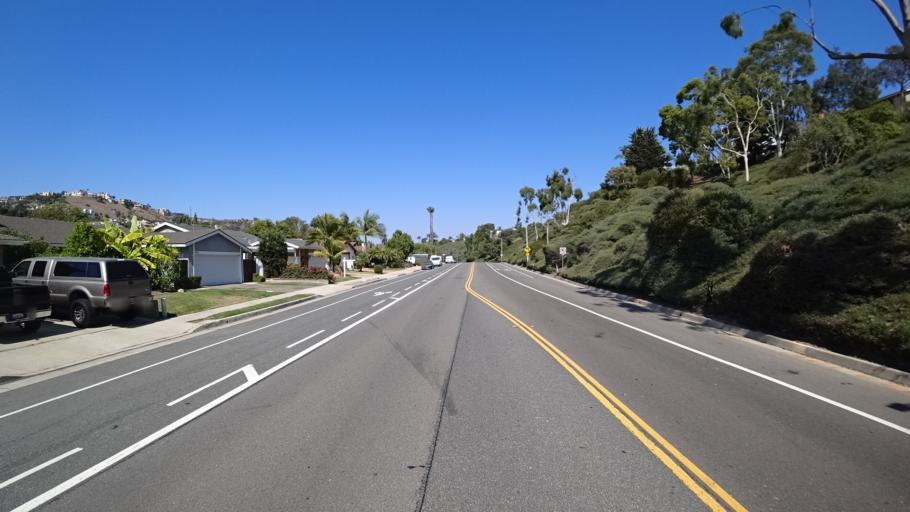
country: US
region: California
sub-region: Orange County
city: San Clemente
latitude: 33.4549
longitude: -117.6420
